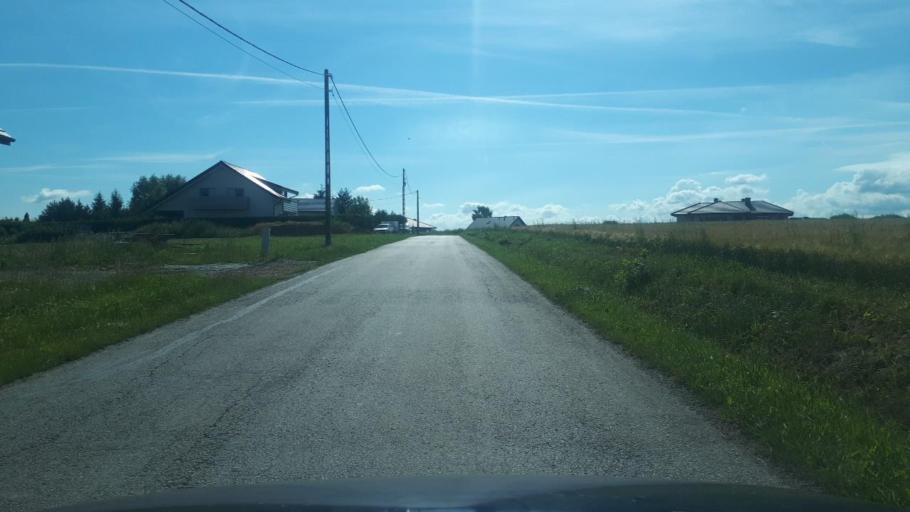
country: PL
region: Silesian Voivodeship
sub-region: Powiat bielski
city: Pisarzowice
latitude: 49.8754
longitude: 19.1252
